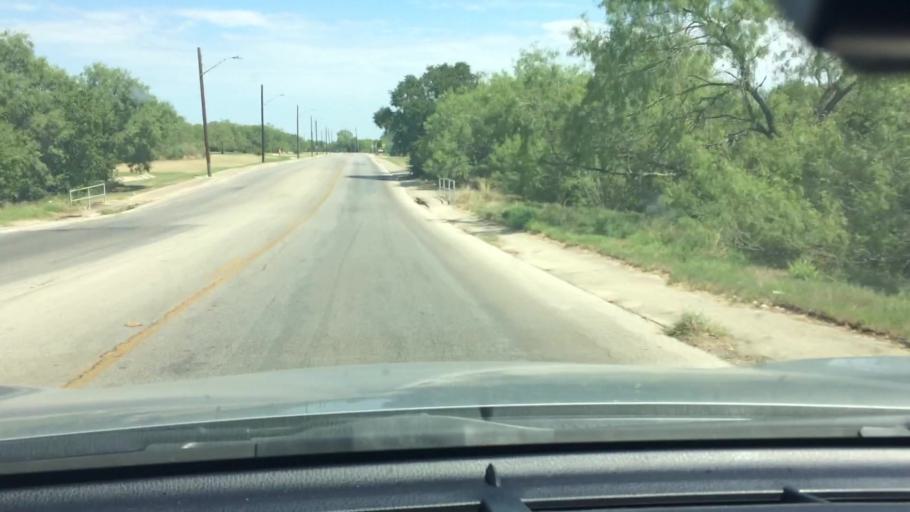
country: US
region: Texas
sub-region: Bexar County
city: San Antonio
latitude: 29.3829
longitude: -98.4305
